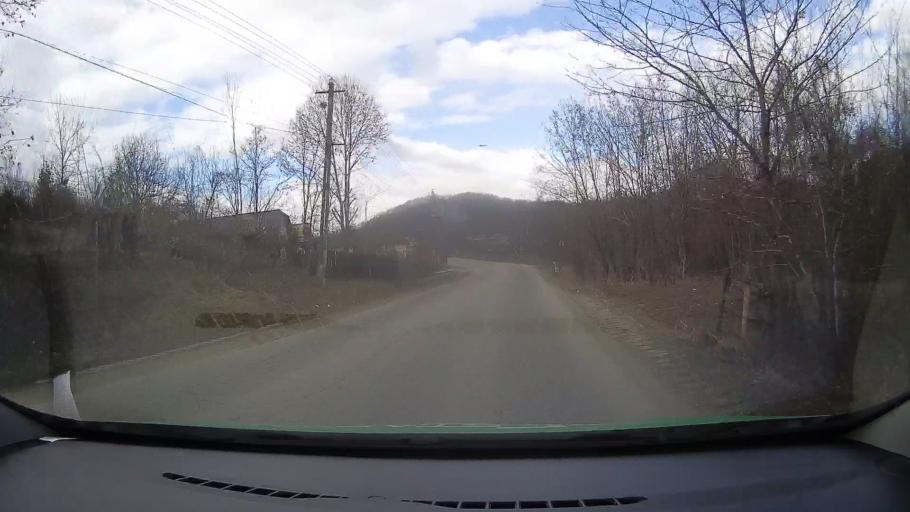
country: RO
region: Dambovita
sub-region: Comuna Visinesti
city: Visinesti
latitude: 45.0657
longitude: 25.5511
